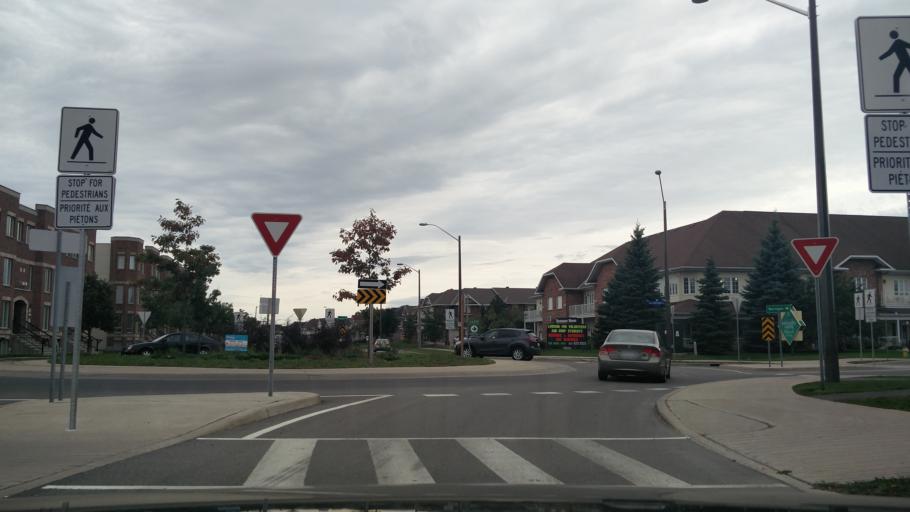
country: CA
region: Ontario
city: Bells Corners
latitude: 45.2785
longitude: -75.7417
